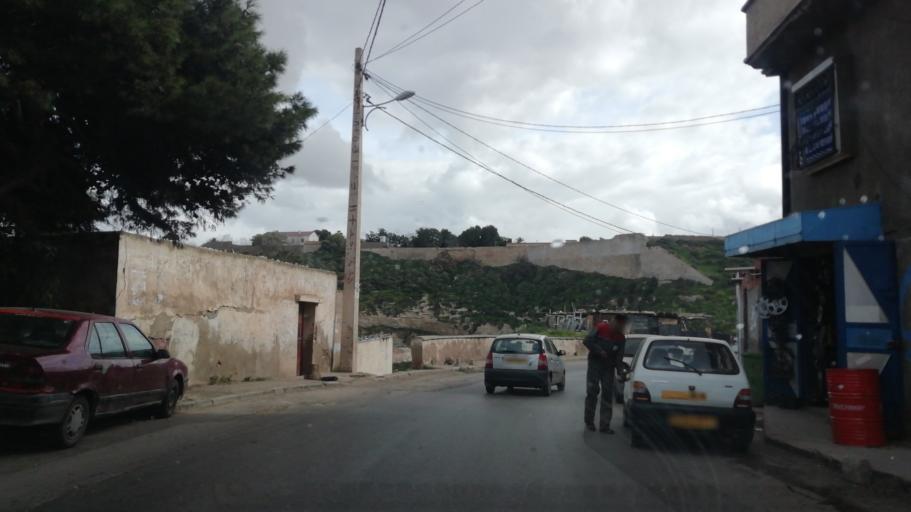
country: DZ
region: Oran
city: Oran
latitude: 35.6963
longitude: -0.6595
